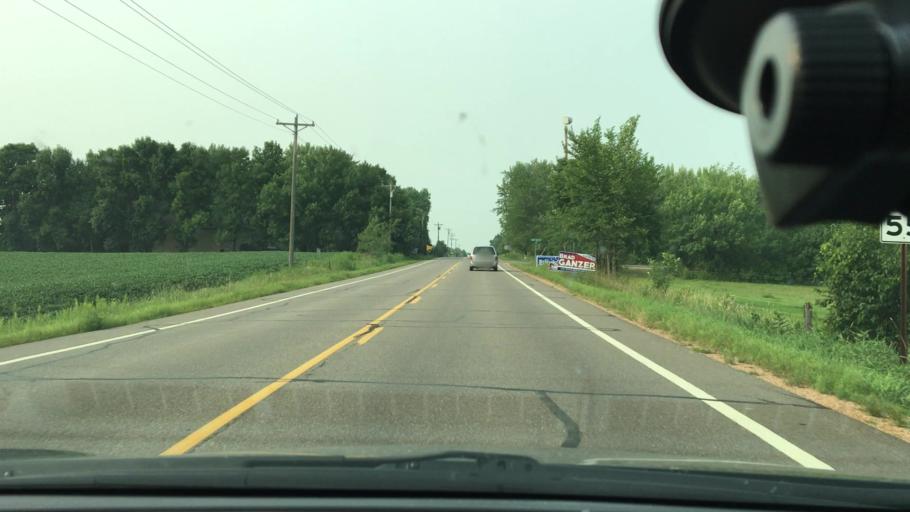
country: US
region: Minnesota
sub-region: Hennepin County
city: Champlin
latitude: 45.1604
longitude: -93.4620
